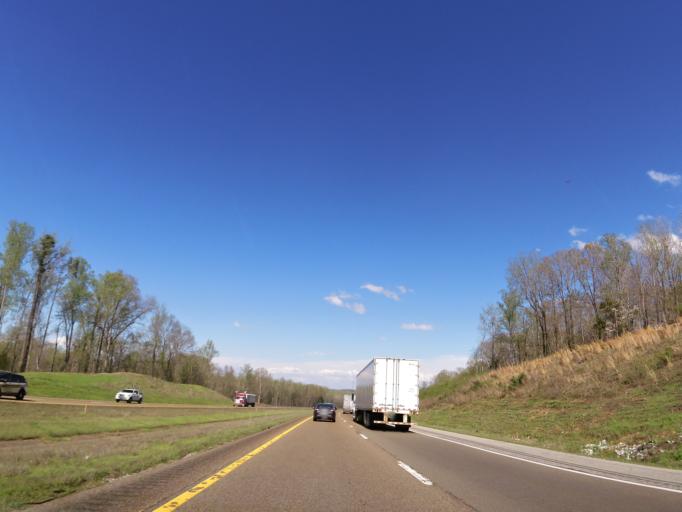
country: US
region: Tennessee
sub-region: Henderson County
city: Lexington
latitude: 35.7422
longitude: -88.5737
